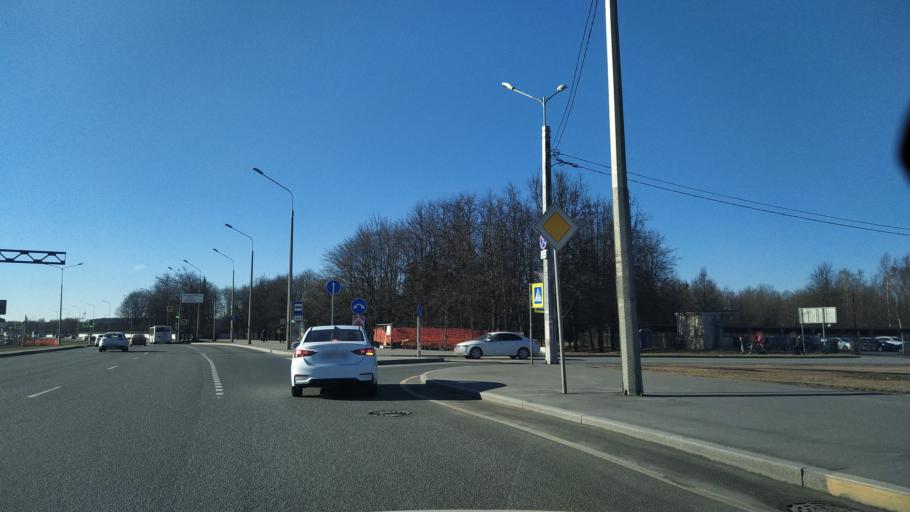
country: RU
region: Leningrad
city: Kalininskiy
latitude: 59.9932
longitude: 30.4277
